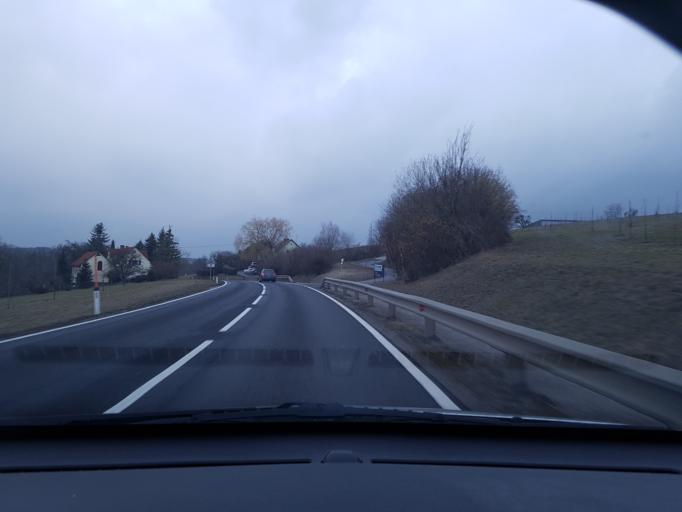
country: AT
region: Upper Austria
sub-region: Politischer Bezirk Linz-Land
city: Ansfelden
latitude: 48.1367
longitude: 14.3303
